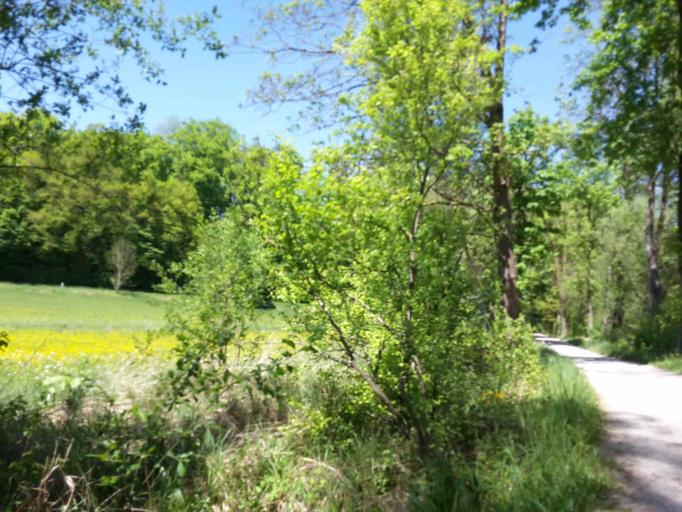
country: DE
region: Bavaria
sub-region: Upper Bavaria
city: Fuerstenfeldbruck
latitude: 48.1595
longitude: 11.2338
